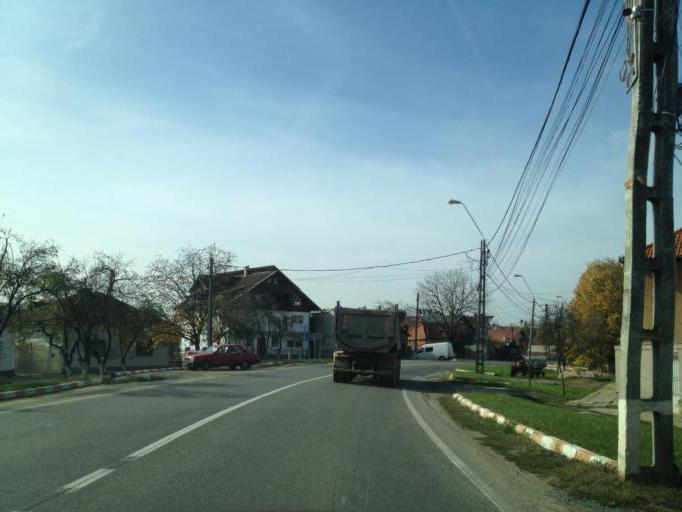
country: RO
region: Timis
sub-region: Comuna Faget
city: Faget
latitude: 45.8566
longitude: 22.1830
